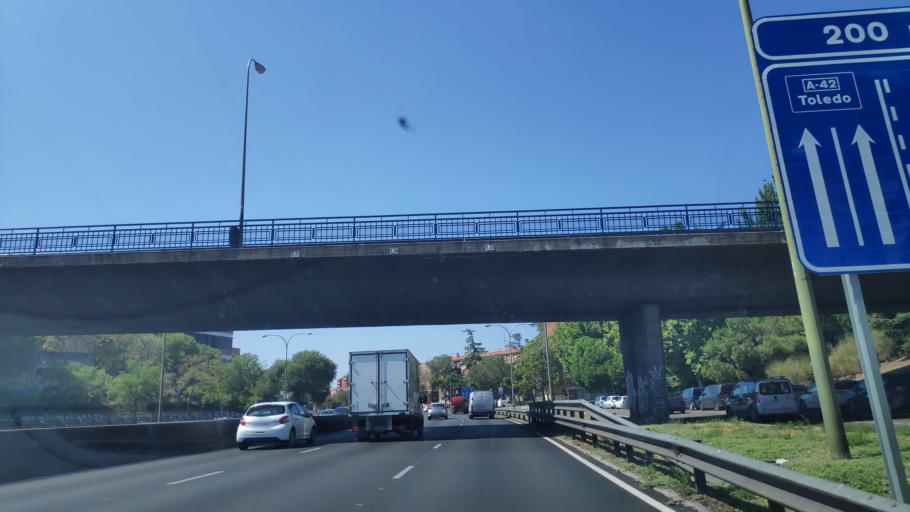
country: ES
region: Madrid
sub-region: Provincia de Madrid
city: Usera
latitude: 40.3904
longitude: -3.7117
